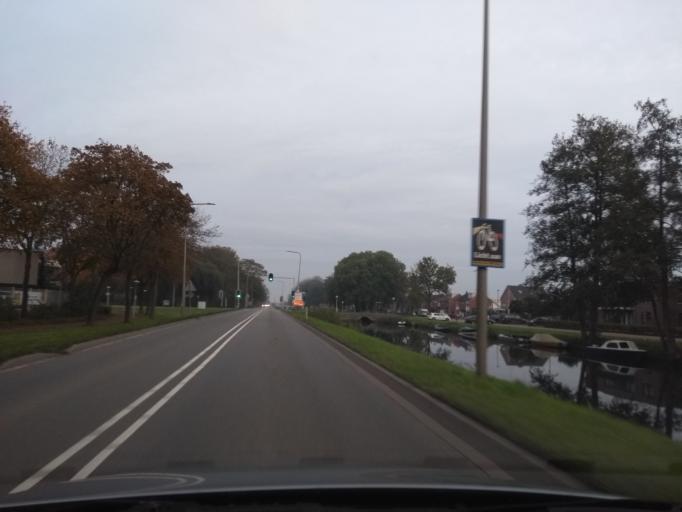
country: NL
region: Overijssel
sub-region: Gemeente Zwartewaterland
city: Hasselt
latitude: 52.5934
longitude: 6.0952
